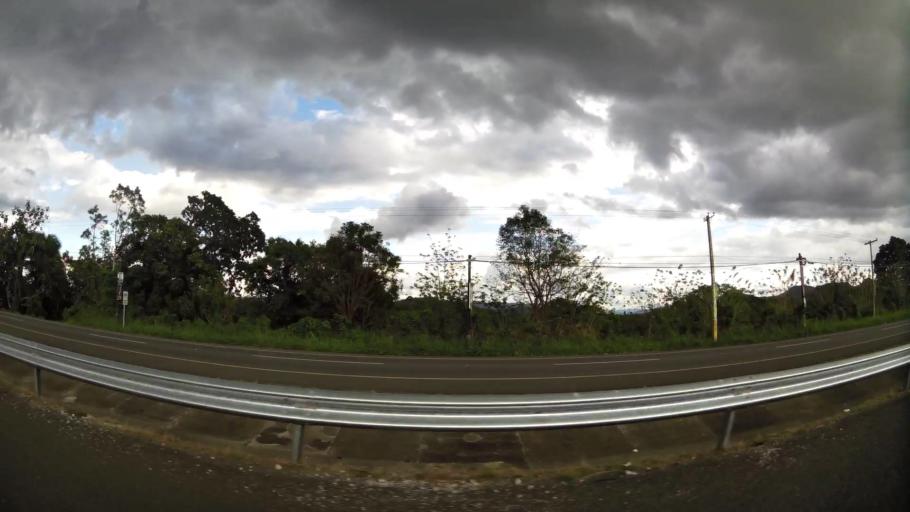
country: DO
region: Monsenor Nouel
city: Sabana del Puerto
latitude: 19.0170
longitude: -70.4452
